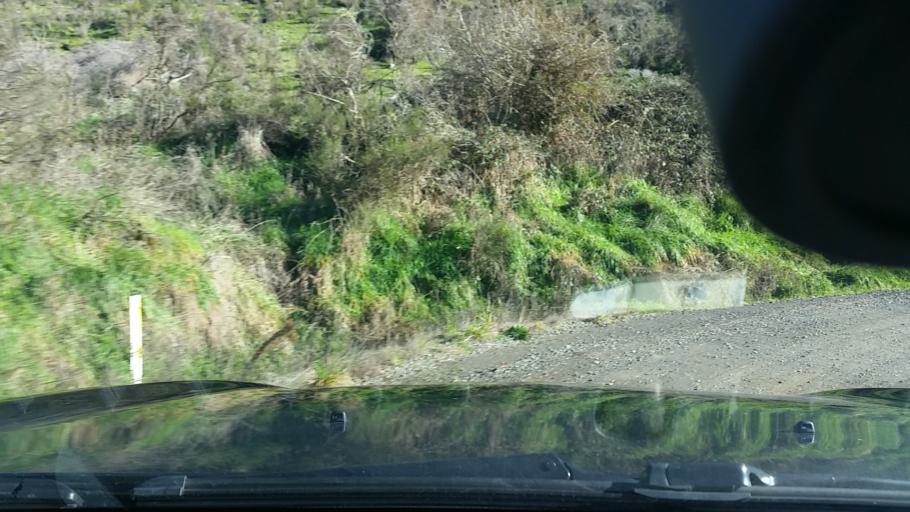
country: NZ
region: Marlborough
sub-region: Marlborough District
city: Blenheim
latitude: -41.6283
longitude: 173.9690
